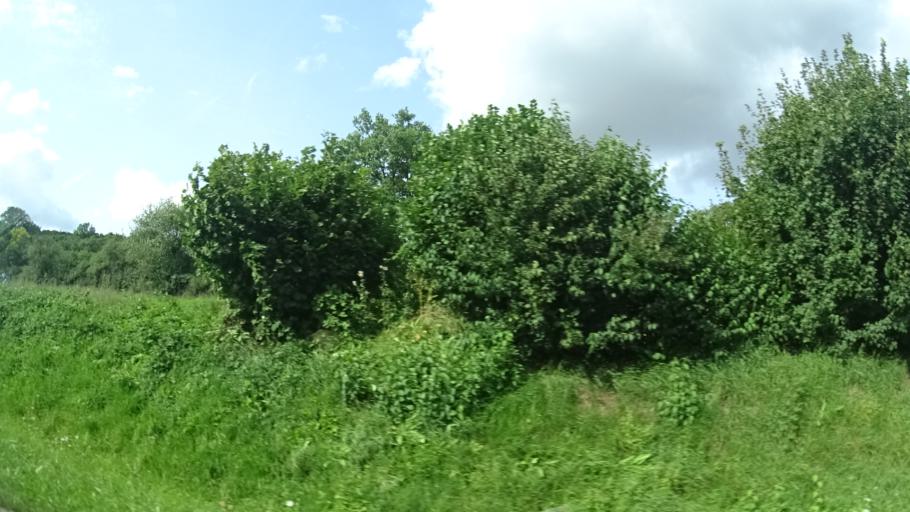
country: DE
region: Bavaria
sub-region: Regierungsbezirk Unterfranken
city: Werneck
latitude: 49.9635
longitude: 10.0514
